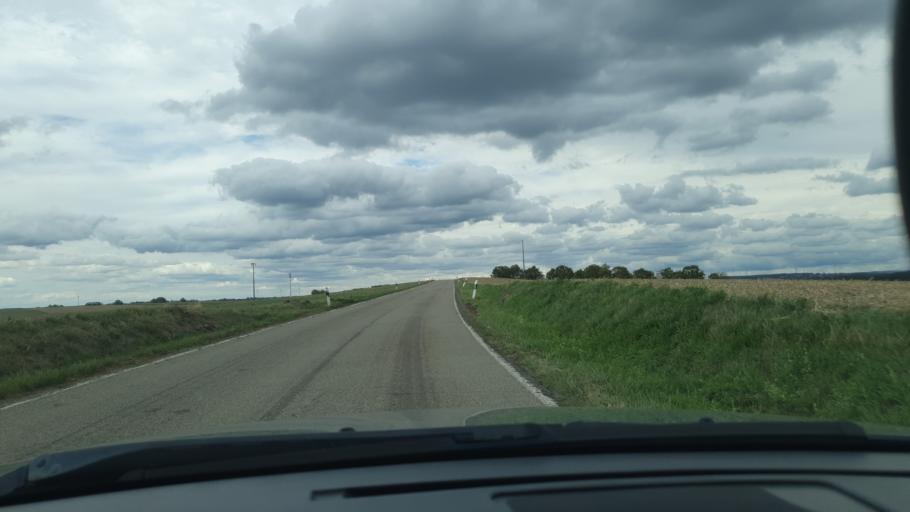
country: DE
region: Rheinland-Pfalz
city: Massweiler
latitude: 49.2697
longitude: 7.5188
